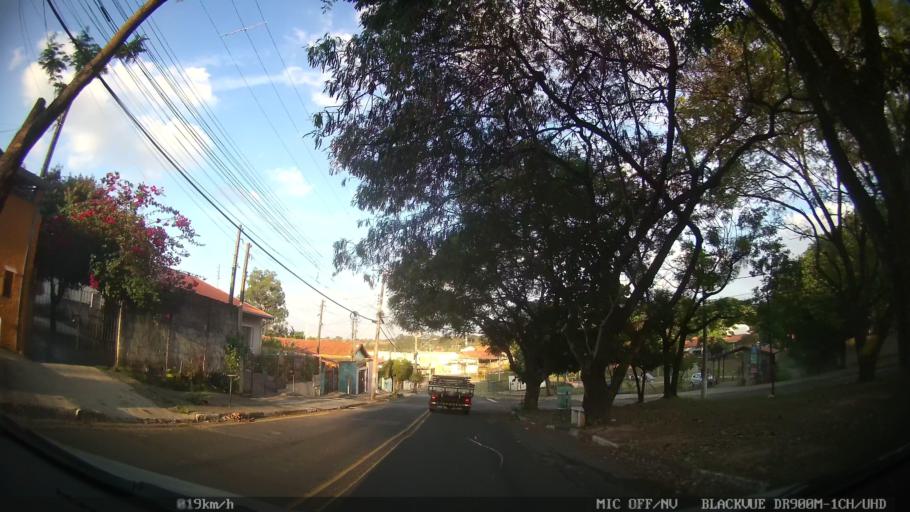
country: BR
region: Sao Paulo
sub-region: Hortolandia
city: Hortolandia
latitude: -22.8960
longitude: -47.1561
